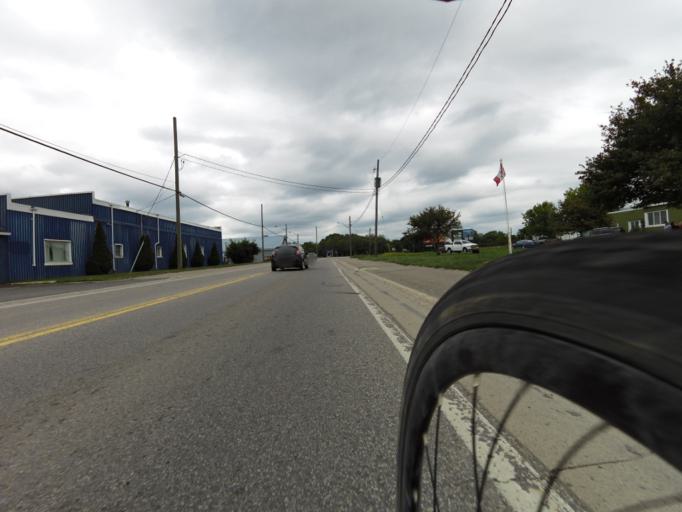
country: CA
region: Ontario
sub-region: Lanark County
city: Smiths Falls
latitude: 44.9118
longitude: -76.0225
